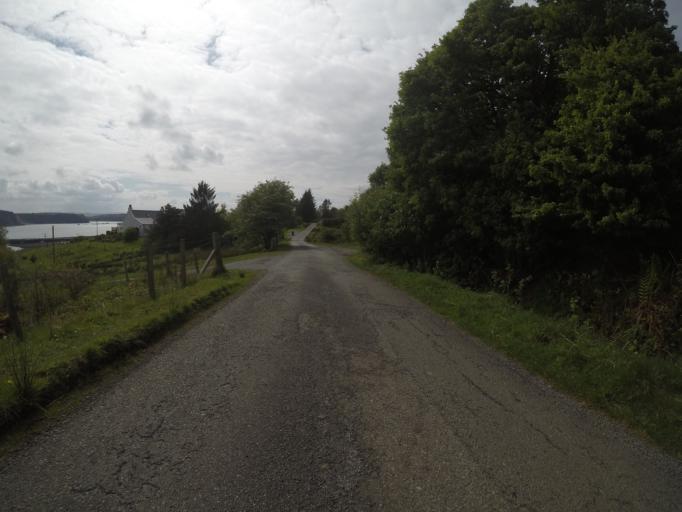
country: GB
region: Scotland
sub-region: Highland
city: Portree
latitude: 57.5919
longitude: -6.3744
